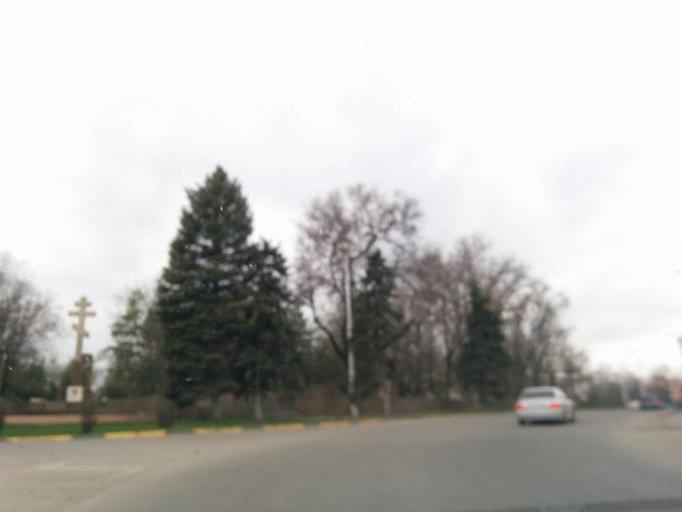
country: RU
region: Rostov
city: Novocherkassk
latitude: 47.4230
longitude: 40.0942
